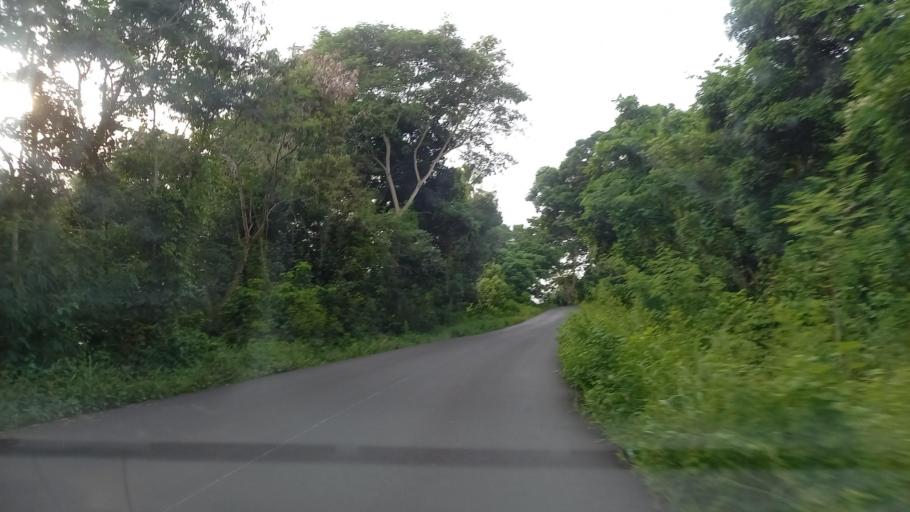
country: YT
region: M'Tsangamouji
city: M'Tsangamouji
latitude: -12.7571
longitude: 45.0670
